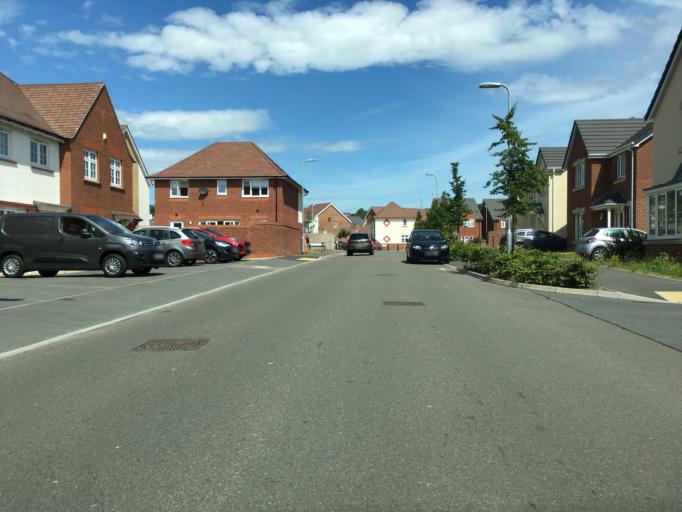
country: GB
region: Wales
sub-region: Newport
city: Newport
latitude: 51.5735
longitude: -3.0020
